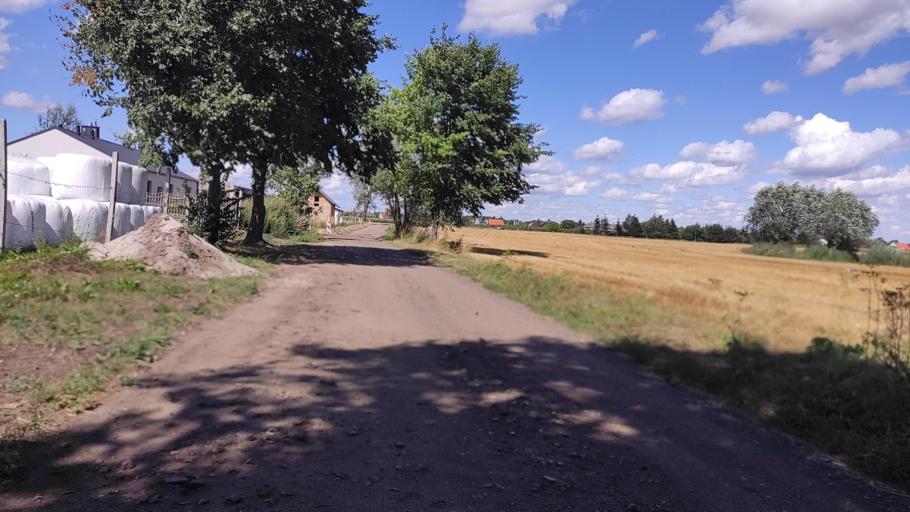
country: PL
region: Greater Poland Voivodeship
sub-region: Powiat poznanski
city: Kleszczewo
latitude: 52.3856
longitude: 17.1504
